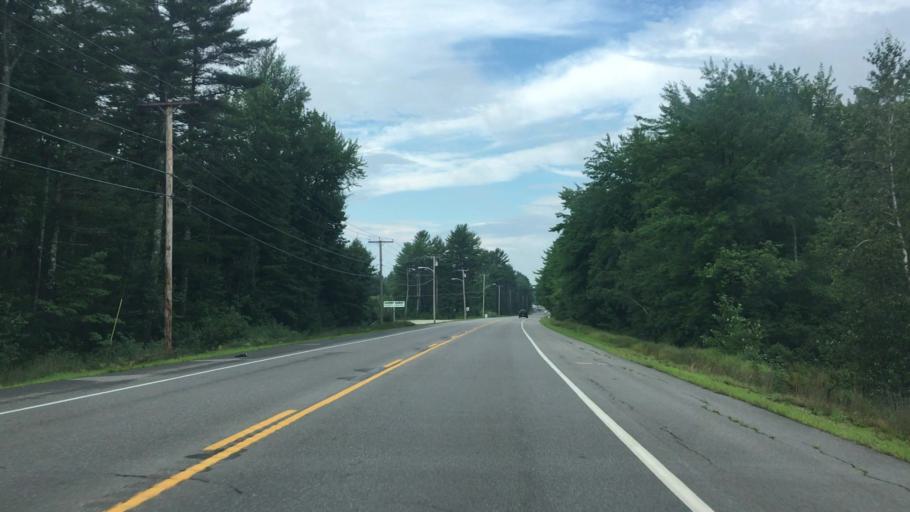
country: US
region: Maine
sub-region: York County
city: Lebanon
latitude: 43.3676
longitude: -70.8988
